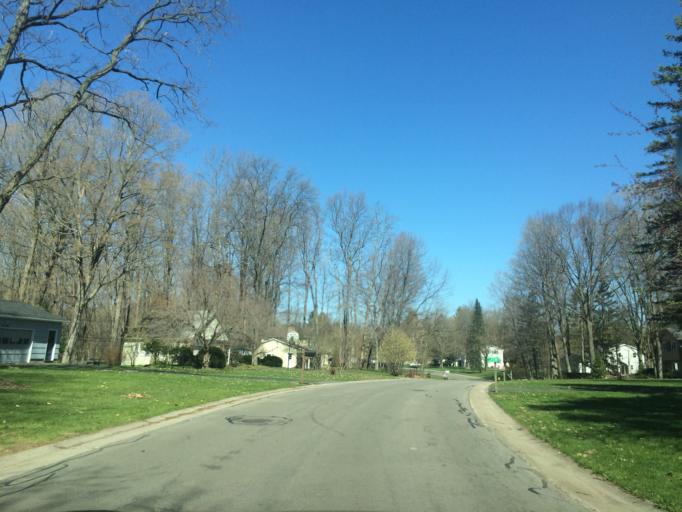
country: US
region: New York
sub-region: Monroe County
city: East Rochester
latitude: 43.0942
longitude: -77.4689
